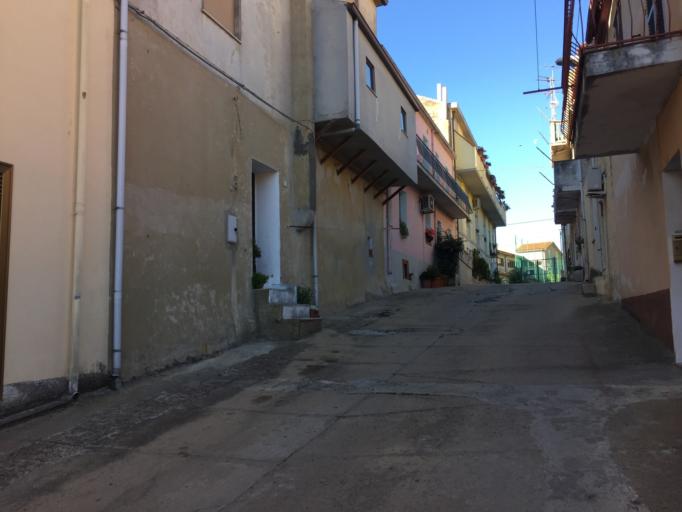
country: IT
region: Sardinia
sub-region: Provincia di Olbia-Tempio
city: Aggius
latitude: 40.9305
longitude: 9.0638
